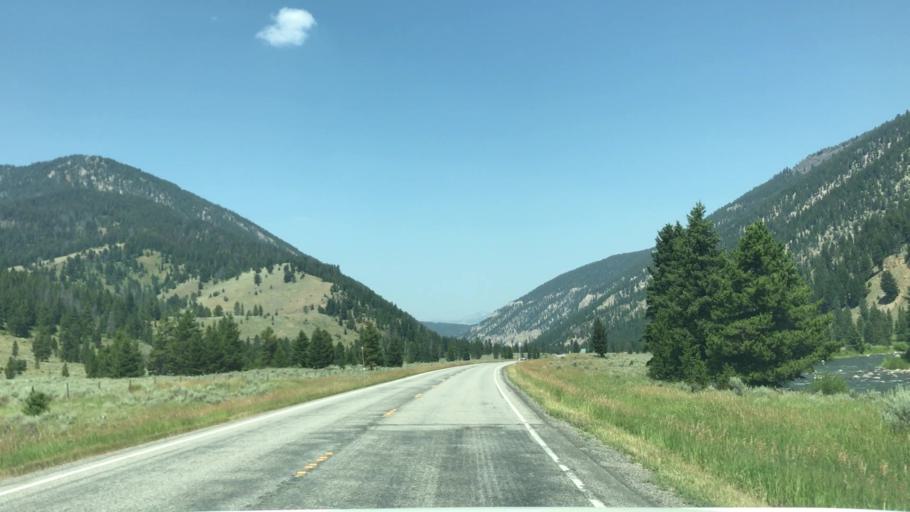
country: US
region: Montana
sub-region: Gallatin County
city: Big Sky
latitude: 45.1057
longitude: -111.2220
